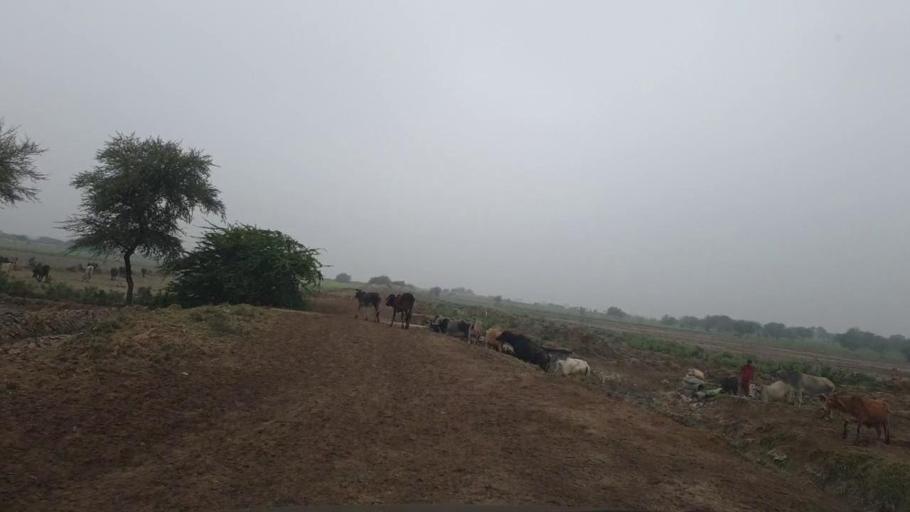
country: PK
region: Sindh
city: Badin
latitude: 24.6292
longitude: 68.6855
